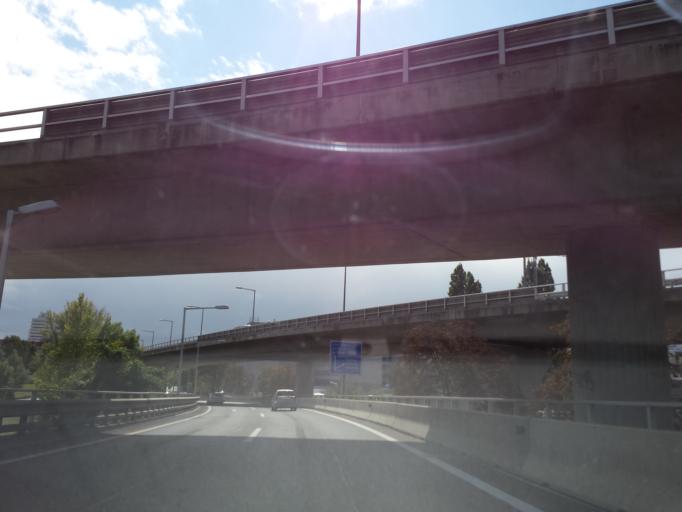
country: AT
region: Vienna
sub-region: Wien Stadt
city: Vienna
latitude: 48.2509
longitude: 16.3719
